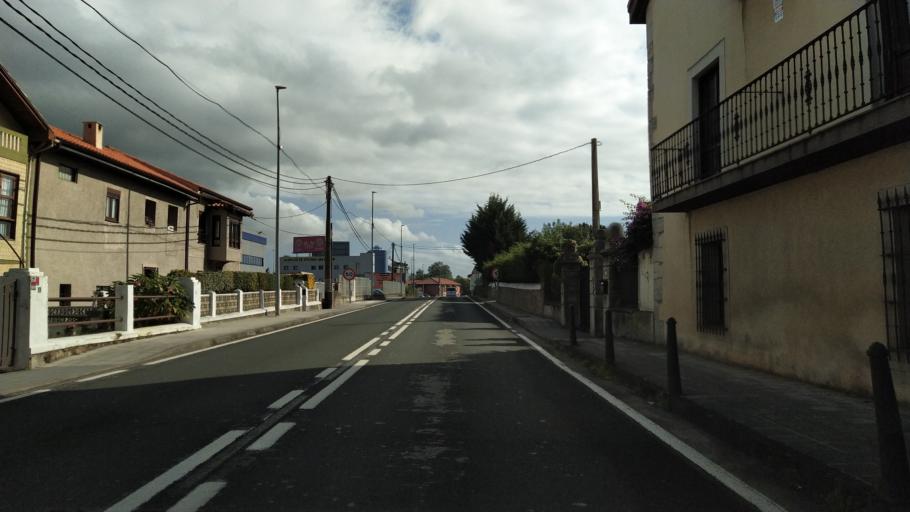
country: ES
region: Cantabria
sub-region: Provincia de Cantabria
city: Santa Cruz de Bezana
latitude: 43.4372
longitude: -3.9024
